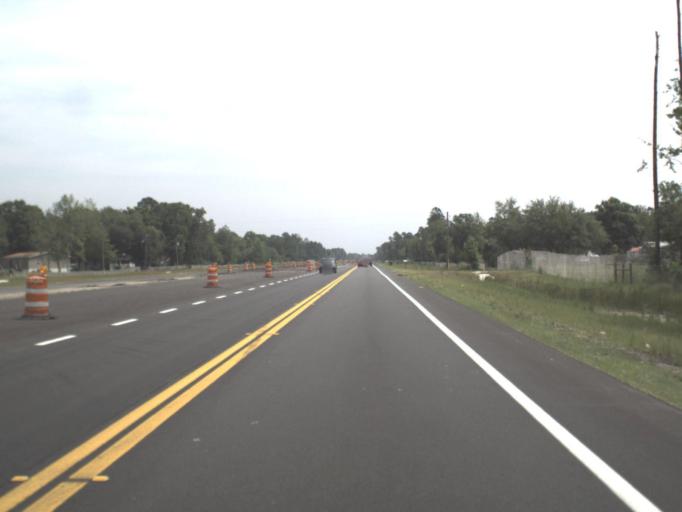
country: US
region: Florida
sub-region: Nassau County
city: Nassau Village-Ratliff
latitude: 30.4489
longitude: -81.9162
